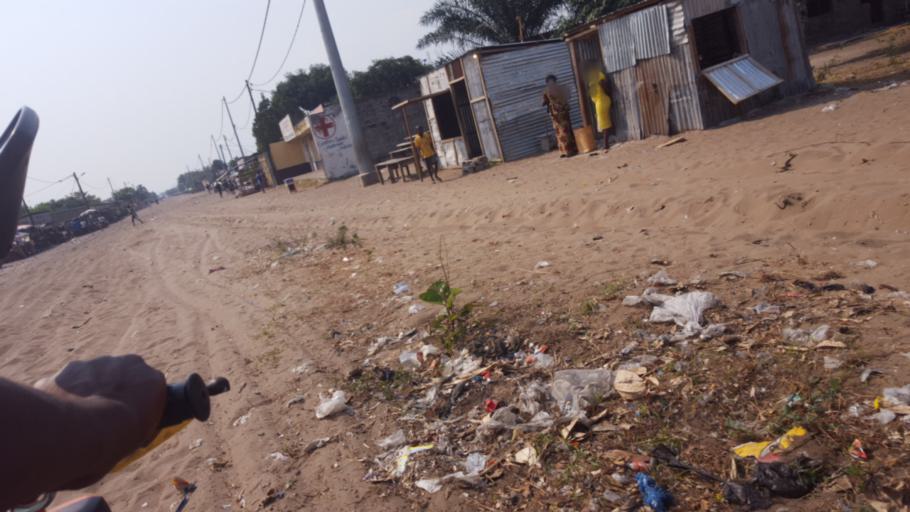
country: CD
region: Kinshasa
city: Masina
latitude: -4.3681
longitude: 15.5143
